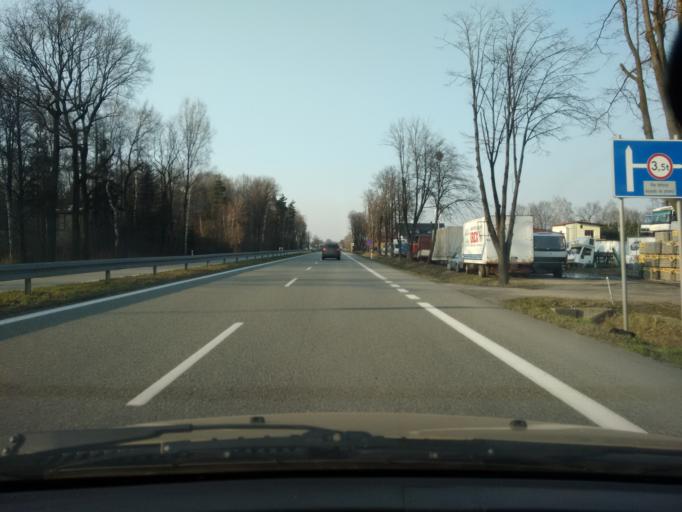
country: PL
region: Silesian Voivodeship
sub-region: Powiat cieszynski
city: Zbytkow
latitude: 49.9097
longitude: 18.7357
